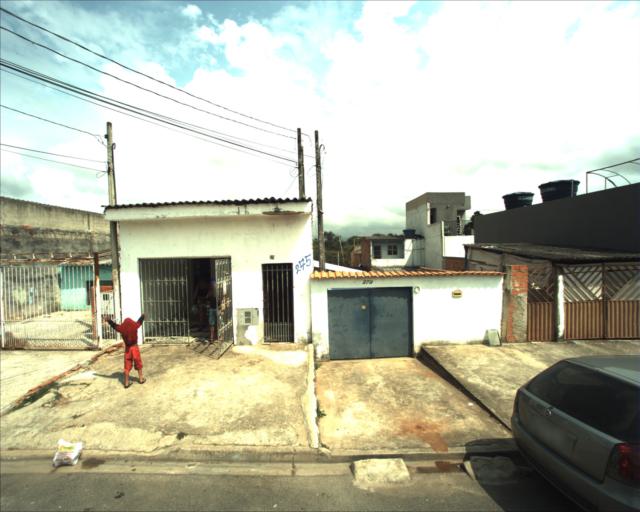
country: BR
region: Sao Paulo
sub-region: Sorocaba
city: Sorocaba
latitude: -23.4307
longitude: -47.5135
